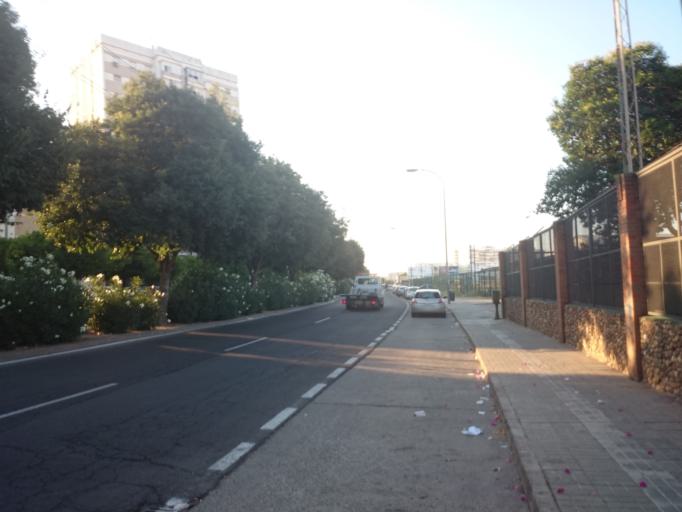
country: ES
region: Andalusia
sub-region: Provincia de Sevilla
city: Sevilla
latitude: 37.3975
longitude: -5.9613
